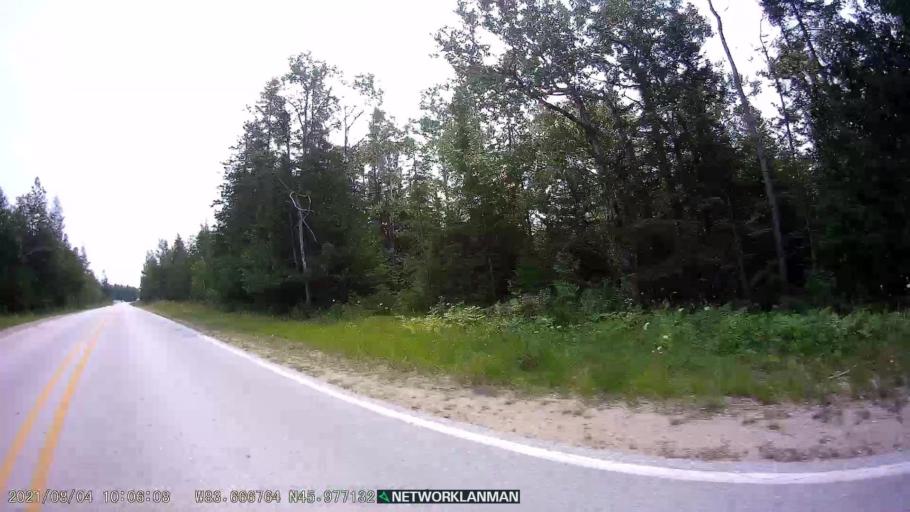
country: CA
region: Ontario
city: Thessalon
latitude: 45.9771
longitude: -83.6665
